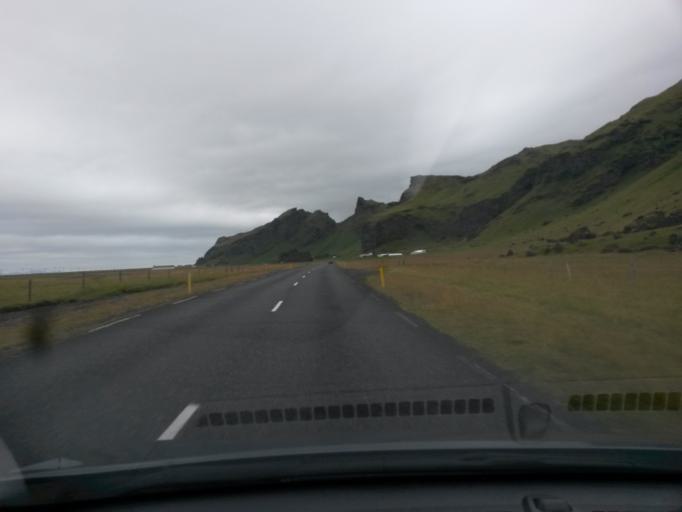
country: IS
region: South
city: Vestmannaeyjar
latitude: 63.5222
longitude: -19.5305
